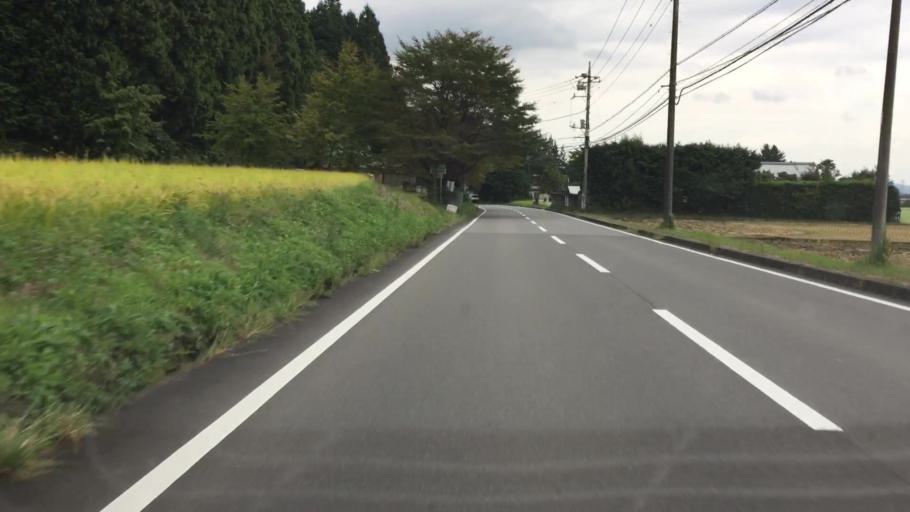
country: JP
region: Tochigi
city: Imaichi
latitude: 36.7667
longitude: 139.6895
